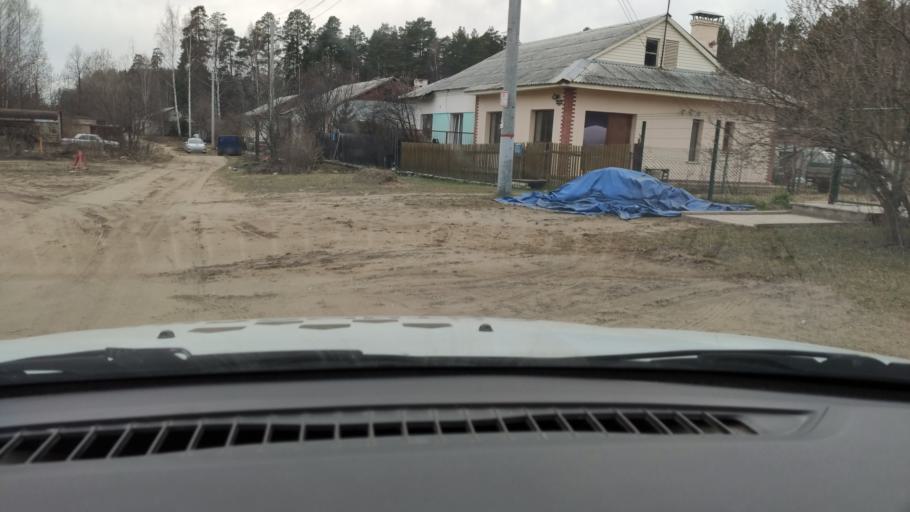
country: RU
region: Perm
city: Perm
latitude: 58.0451
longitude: 56.2051
